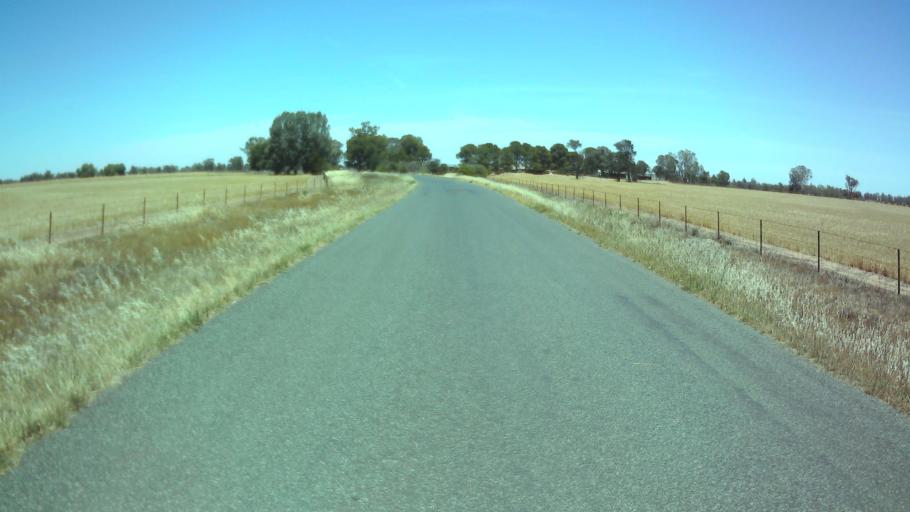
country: AU
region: New South Wales
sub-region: Weddin
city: Grenfell
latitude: -34.0445
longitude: 147.7846
